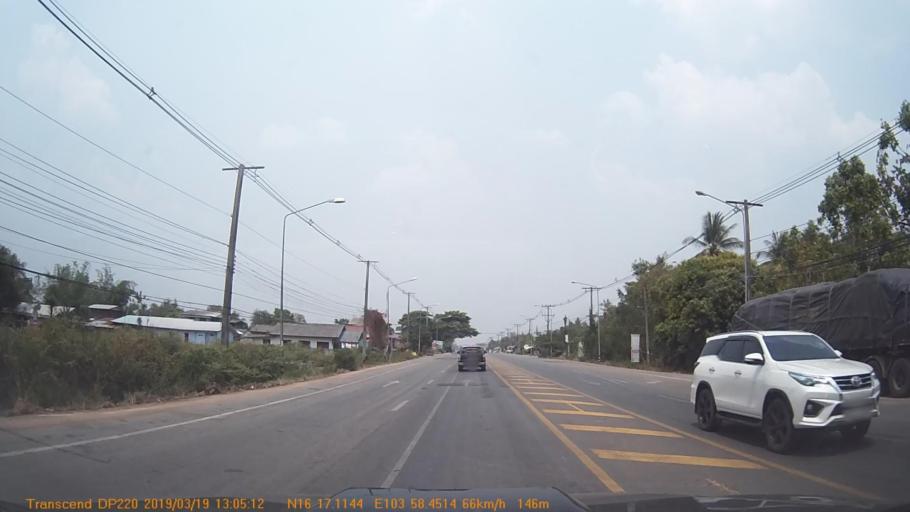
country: TH
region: Roi Et
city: Waeng
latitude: 16.2854
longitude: 103.9742
